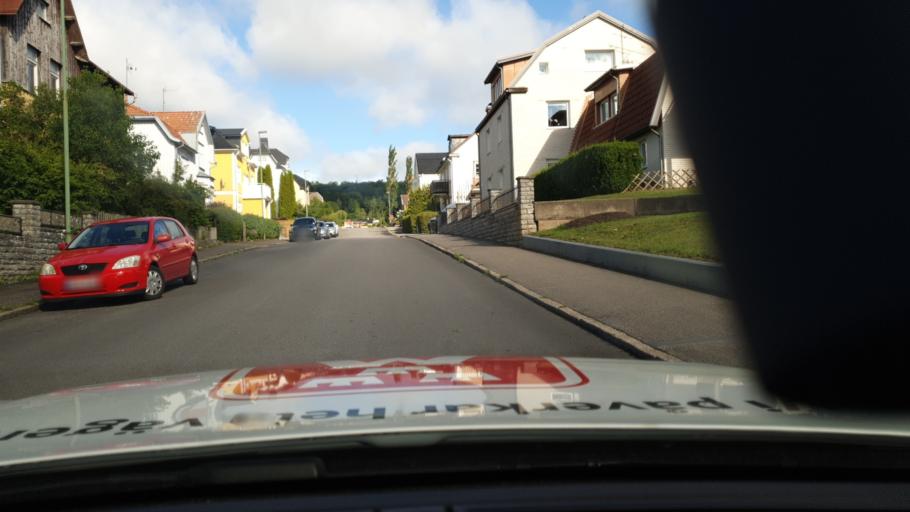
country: SE
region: Vaestra Goetaland
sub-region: Falkopings Kommun
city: Falkoeping
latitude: 58.1754
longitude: 13.5492
